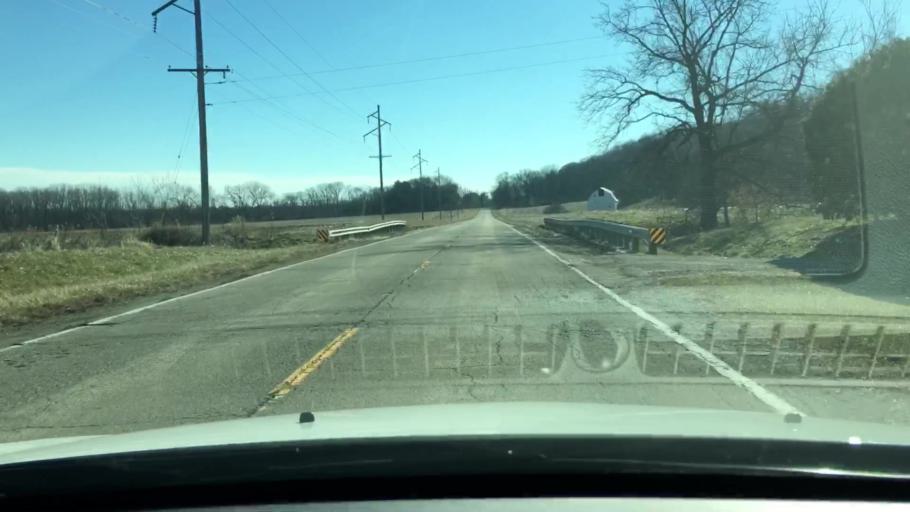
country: US
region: Illinois
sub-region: Fulton County
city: Astoria
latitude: 40.2112
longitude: -90.2065
